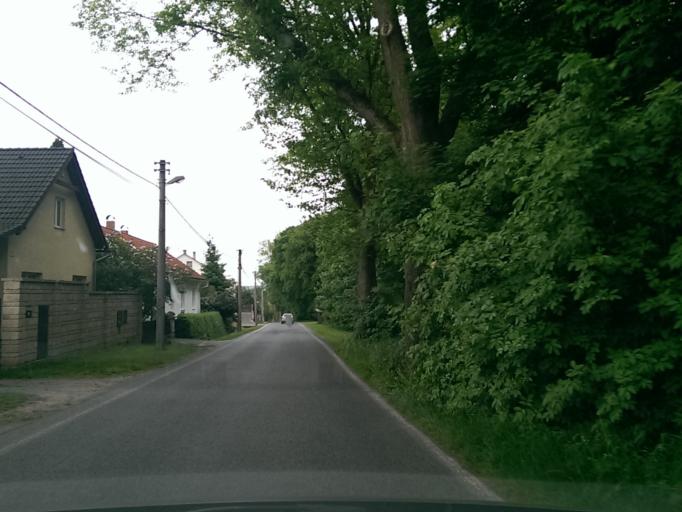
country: CZ
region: Central Bohemia
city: Bakov nad Jizerou
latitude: 50.4854
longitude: 14.9178
